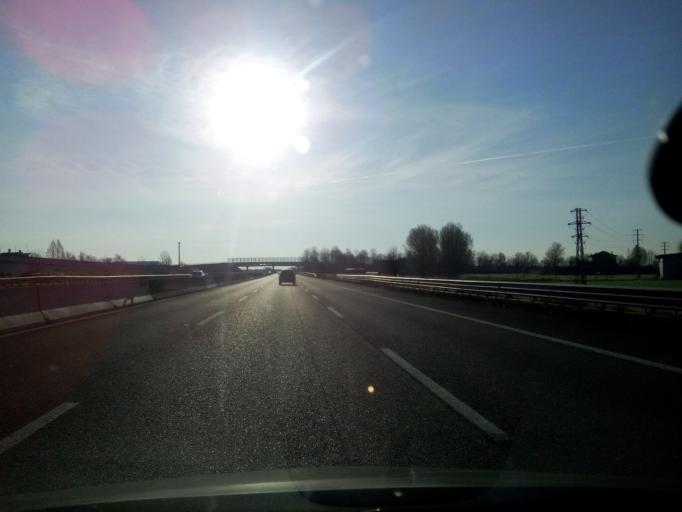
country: IT
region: Emilia-Romagna
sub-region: Provincia di Parma
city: Fontanellato
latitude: 44.8776
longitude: 10.1639
